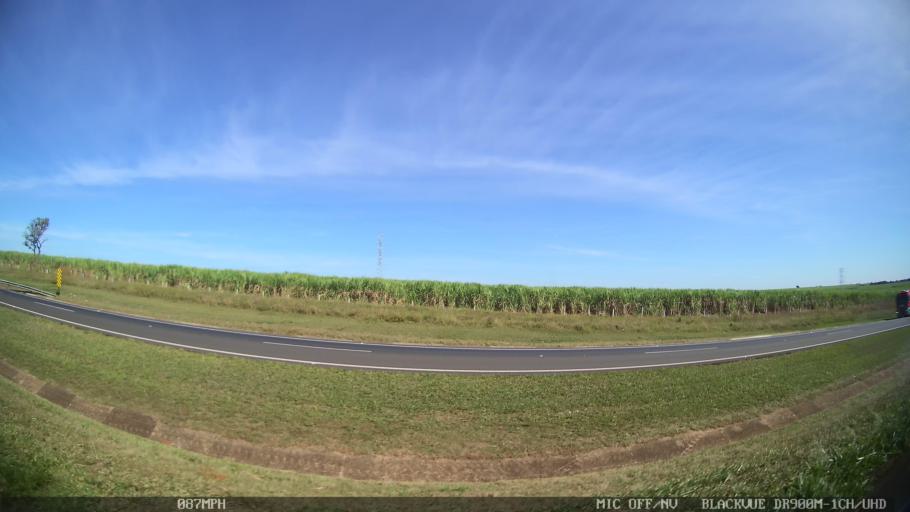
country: BR
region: Sao Paulo
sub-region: Porto Ferreira
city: Porto Ferreira
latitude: -21.9225
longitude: -47.4716
